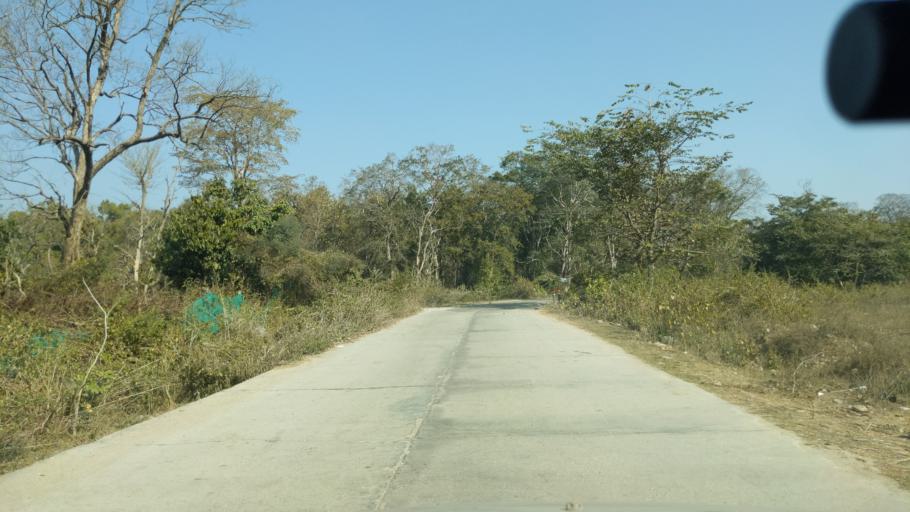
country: IN
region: Uttarakhand
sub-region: Naini Tal
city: Ramnagar
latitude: 29.4104
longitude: 79.1369
